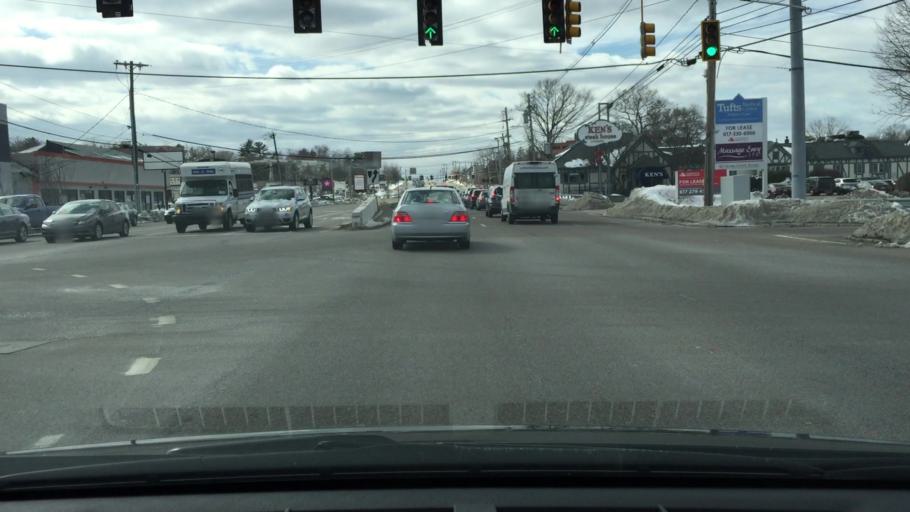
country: US
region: Massachusetts
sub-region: Middlesex County
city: Framingham
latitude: 42.2988
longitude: -71.3967
